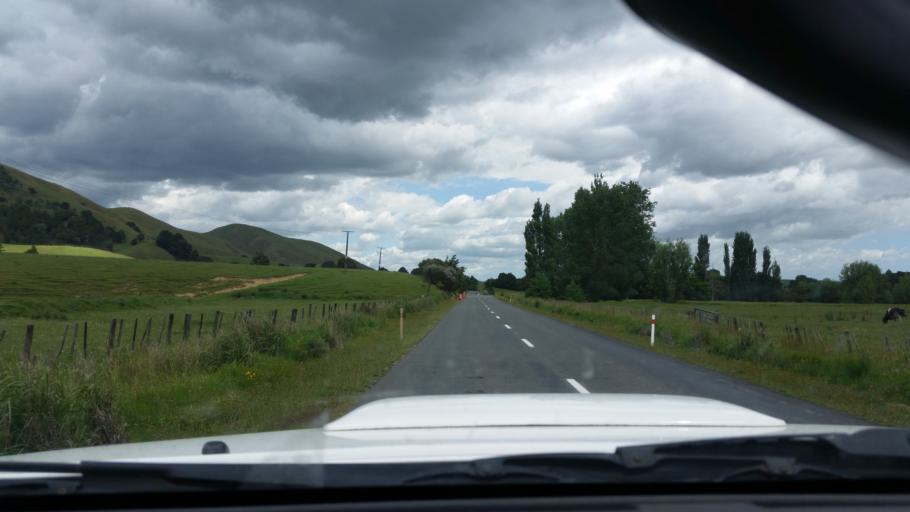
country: NZ
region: Northland
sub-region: Kaipara District
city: Dargaville
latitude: -35.8046
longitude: 173.9203
